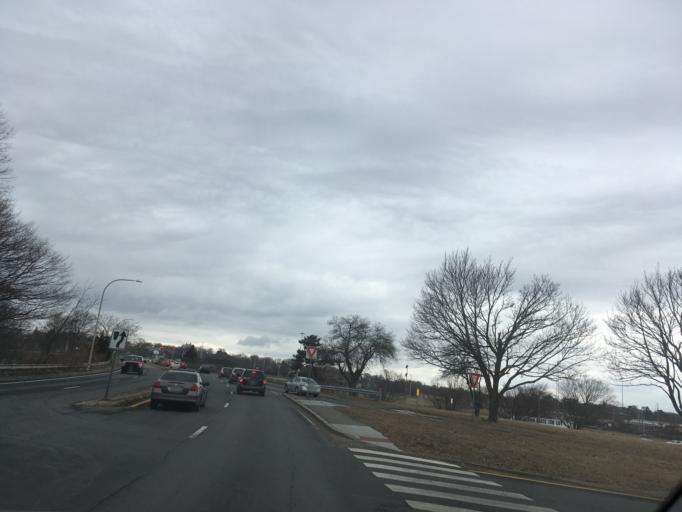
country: US
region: Rhode Island
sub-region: Providence County
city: Providence
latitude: 41.8549
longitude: -71.4046
